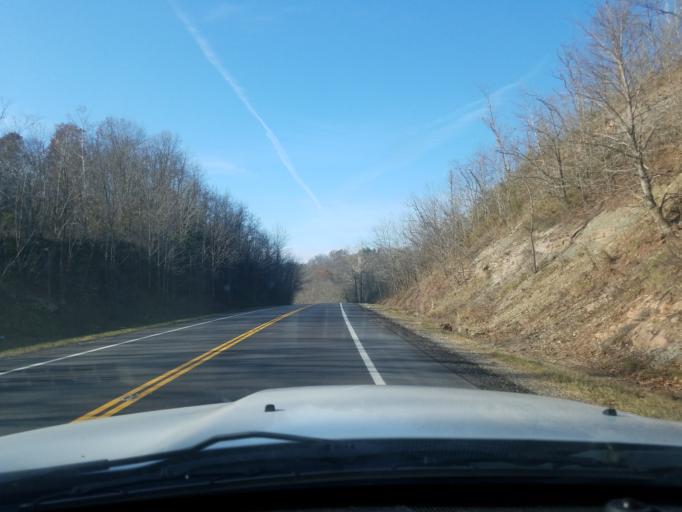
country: US
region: Ohio
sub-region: Washington County
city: Marietta
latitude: 39.4051
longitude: -81.4790
